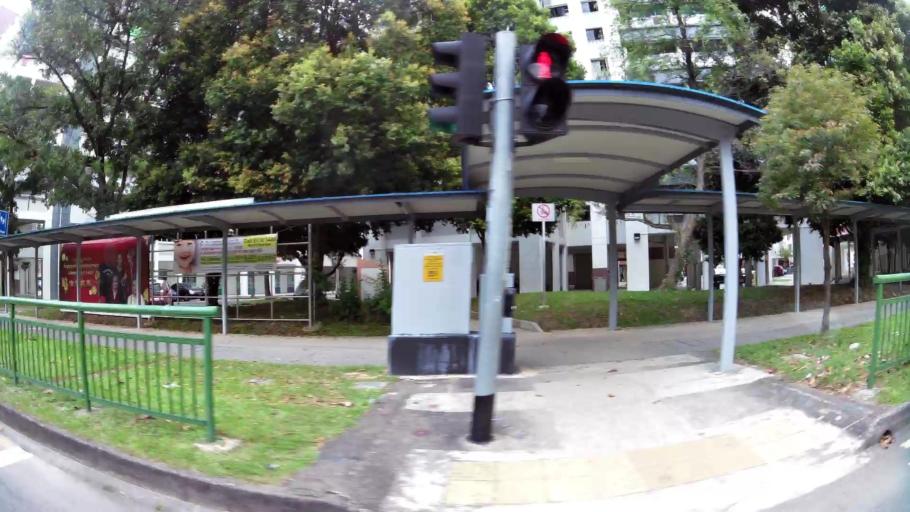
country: MY
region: Johor
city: Kampung Pasir Gudang Baru
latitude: 1.4195
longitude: 103.8321
